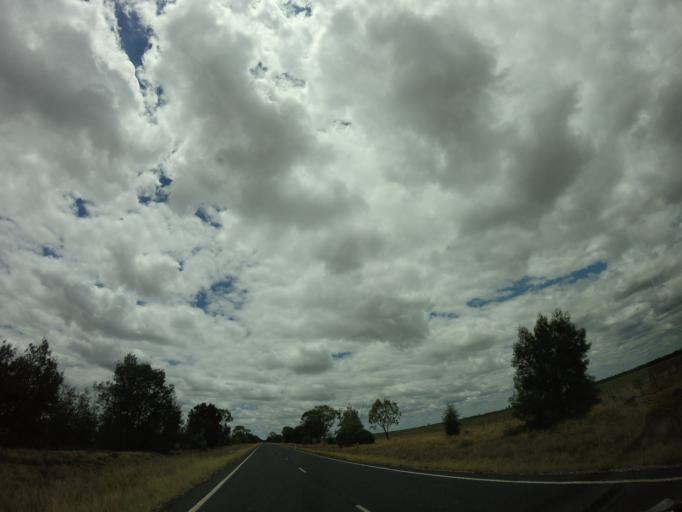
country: AU
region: Queensland
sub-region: Goondiwindi
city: Goondiwindi
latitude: -28.1683
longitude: 150.5183
